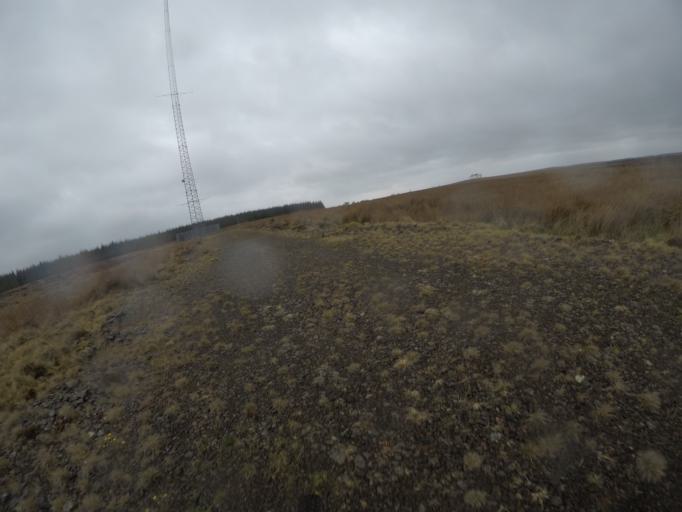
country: GB
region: Scotland
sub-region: East Ayrshire
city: Newmilns
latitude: 55.6348
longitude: -4.3315
